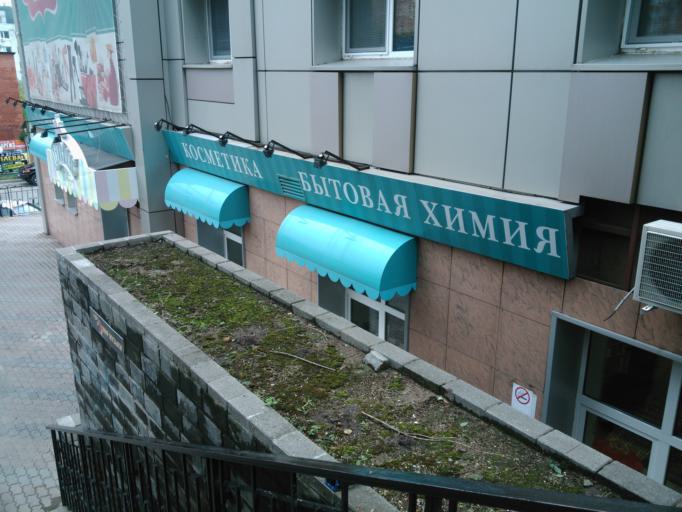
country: RU
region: Primorskiy
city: Vladivostok
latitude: 43.1303
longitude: 131.8923
